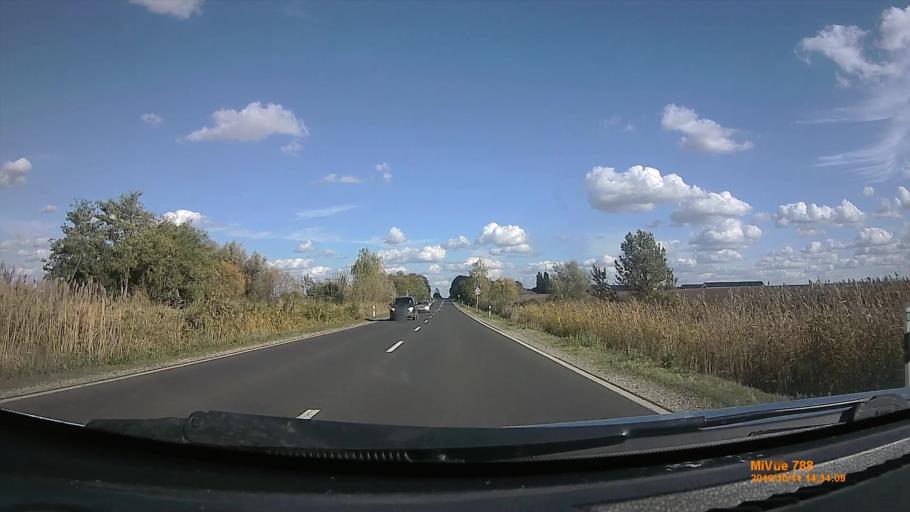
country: HU
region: Hajdu-Bihar
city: Ebes
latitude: 47.5610
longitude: 21.4691
